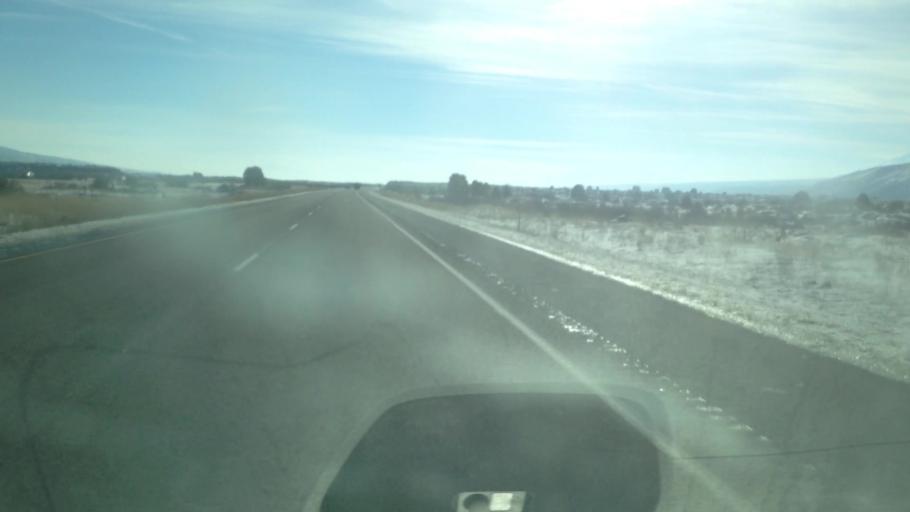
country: US
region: Idaho
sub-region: Bannock County
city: Pocatello
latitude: 42.7480
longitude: -112.2268
